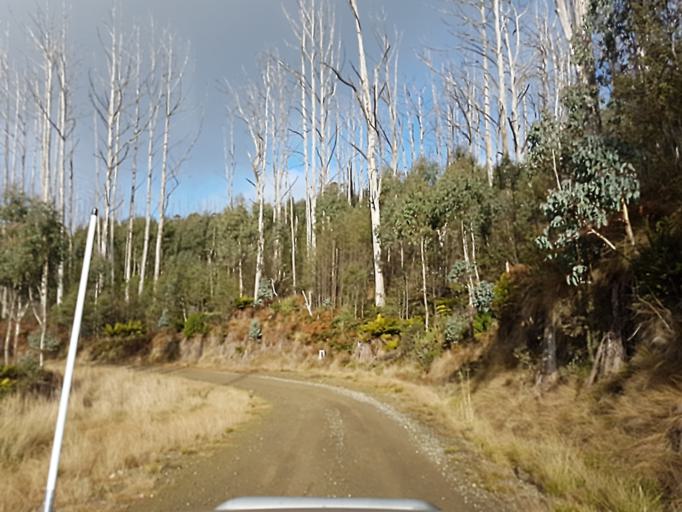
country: AU
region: Victoria
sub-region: Yarra Ranges
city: Millgrove
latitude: -37.5319
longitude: 145.8215
